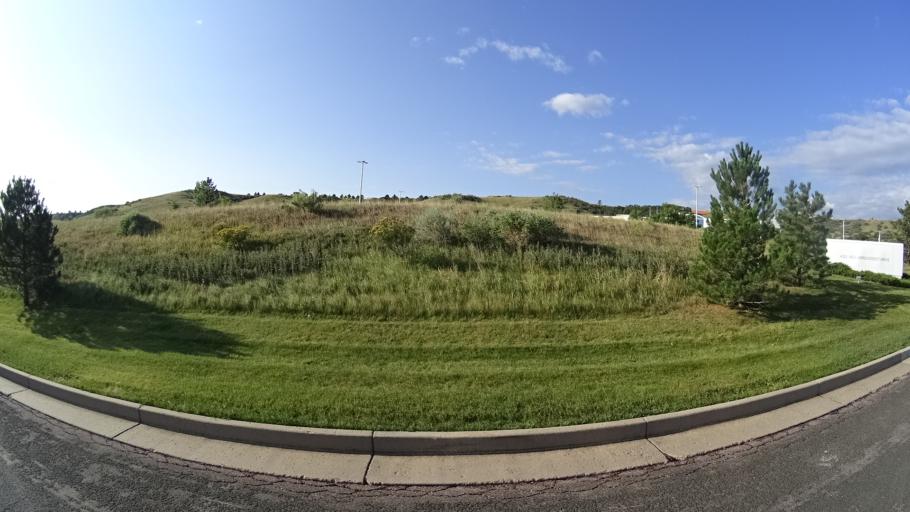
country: US
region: Colorado
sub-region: El Paso County
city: Manitou Springs
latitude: 38.8955
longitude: -104.8688
